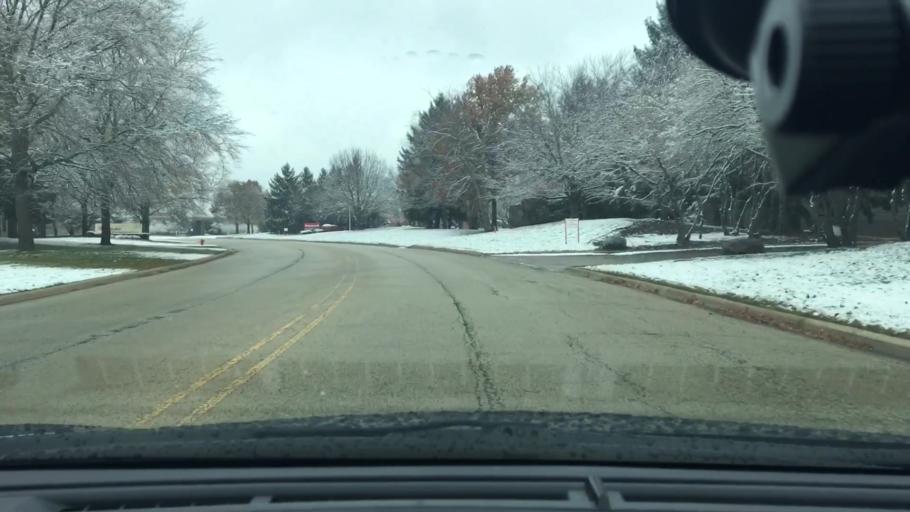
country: US
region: Illinois
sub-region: Lake County
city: Lincolnshire
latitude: 42.1896
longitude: -87.9358
